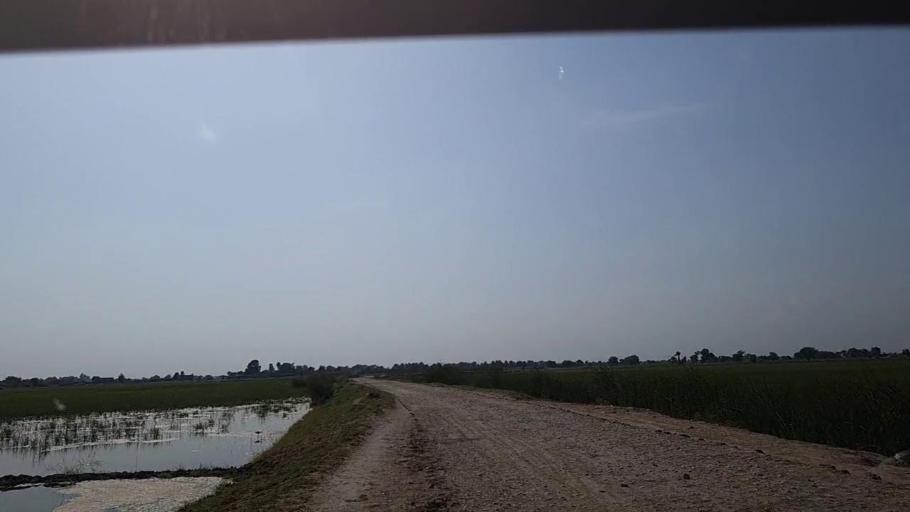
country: PK
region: Sindh
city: Khanpur
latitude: 27.8515
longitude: 69.3628
